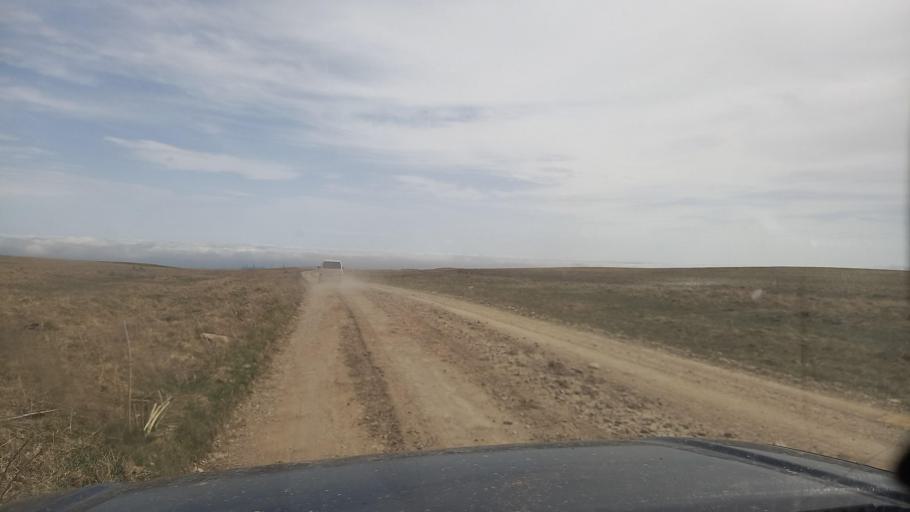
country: RU
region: Stavropol'skiy
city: Kislovodsk
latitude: 43.7522
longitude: 42.7154
